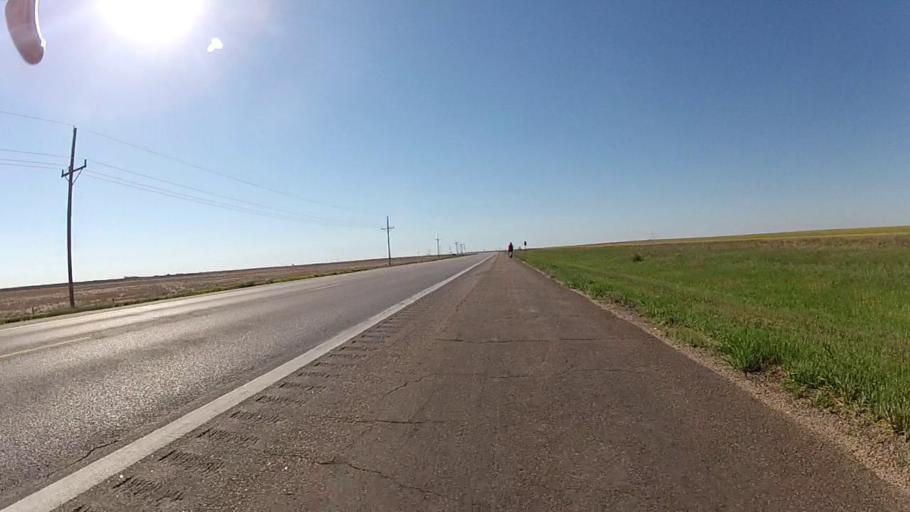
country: US
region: Kansas
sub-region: Ford County
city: Dodge City
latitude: 37.5907
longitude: -99.6888
